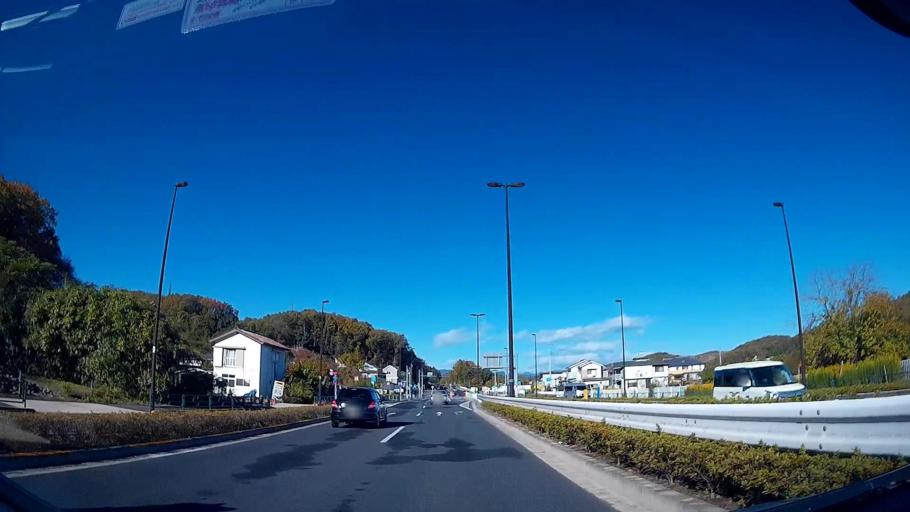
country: JP
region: Tokyo
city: Fussa
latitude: 35.6969
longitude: 139.3199
